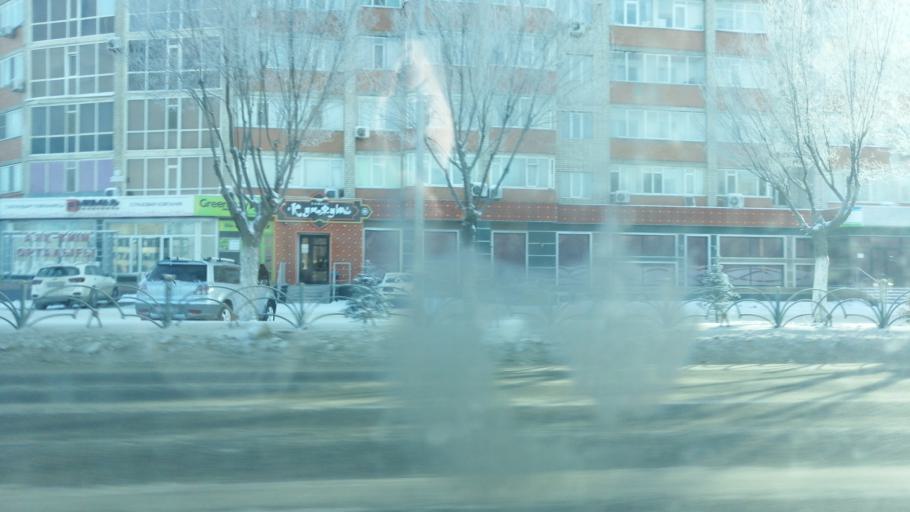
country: KZ
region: Aqtoebe
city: Aqtobe
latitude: 50.2922
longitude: 57.1682
